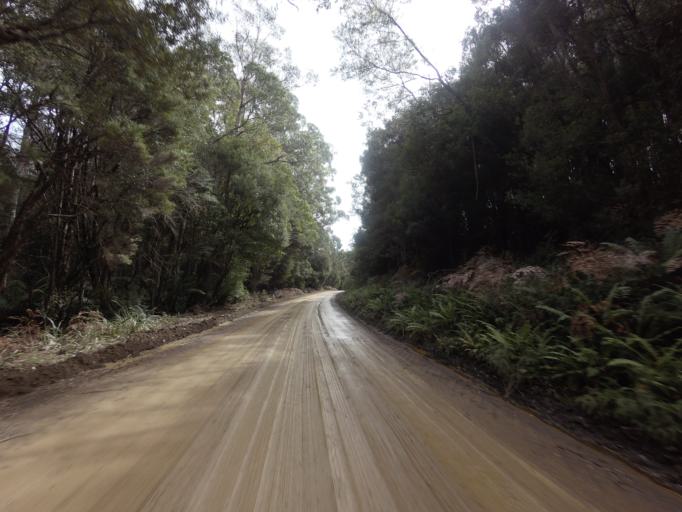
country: AU
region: Tasmania
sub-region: Huon Valley
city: Geeveston
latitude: -43.4073
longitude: 146.8691
